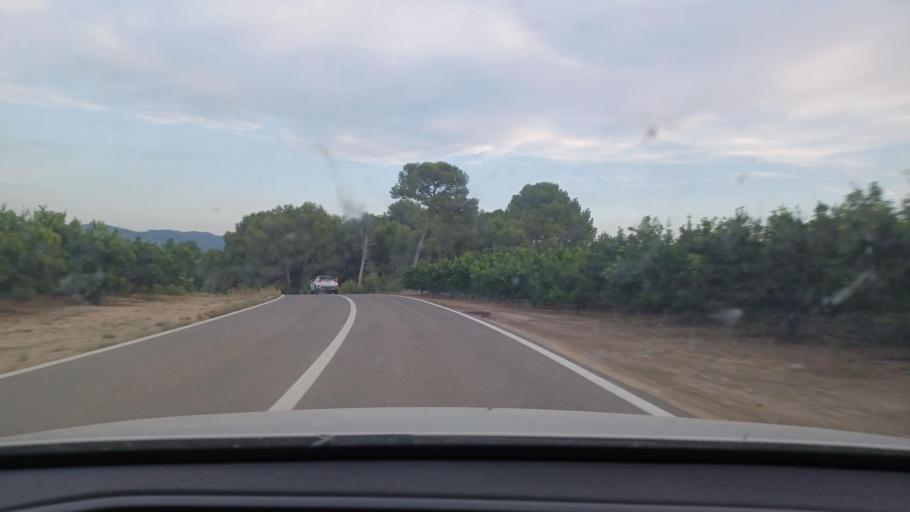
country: ES
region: Catalonia
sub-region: Provincia de Tarragona
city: Santa Barbara
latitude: 40.7170
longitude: 0.4680
